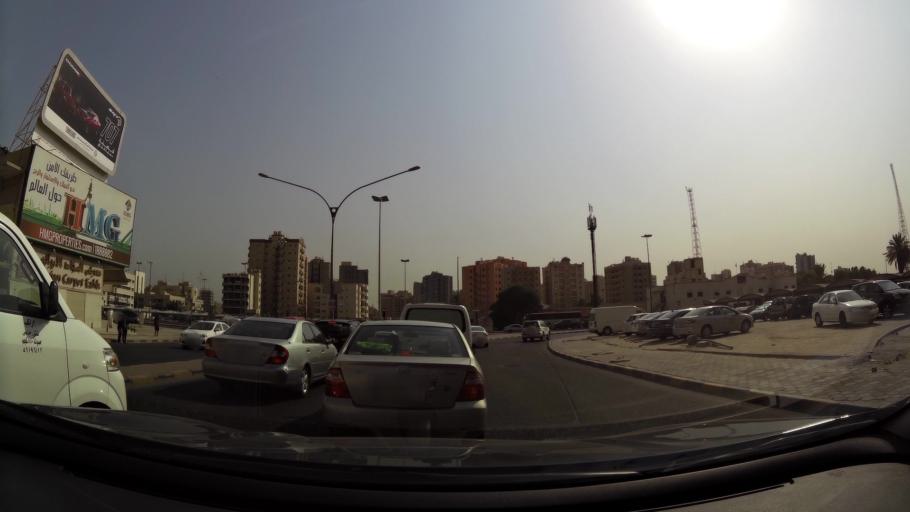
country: KW
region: Muhafazat Hawalli
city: As Salimiyah
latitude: 29.3336
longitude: 48.0540
